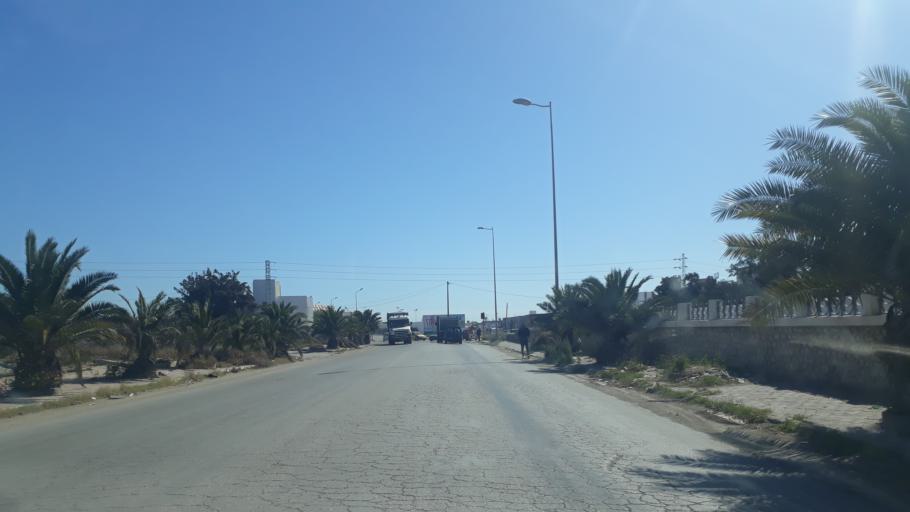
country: TN
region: Safaqis
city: Sfax
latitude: 34.7270
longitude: 10.7539
